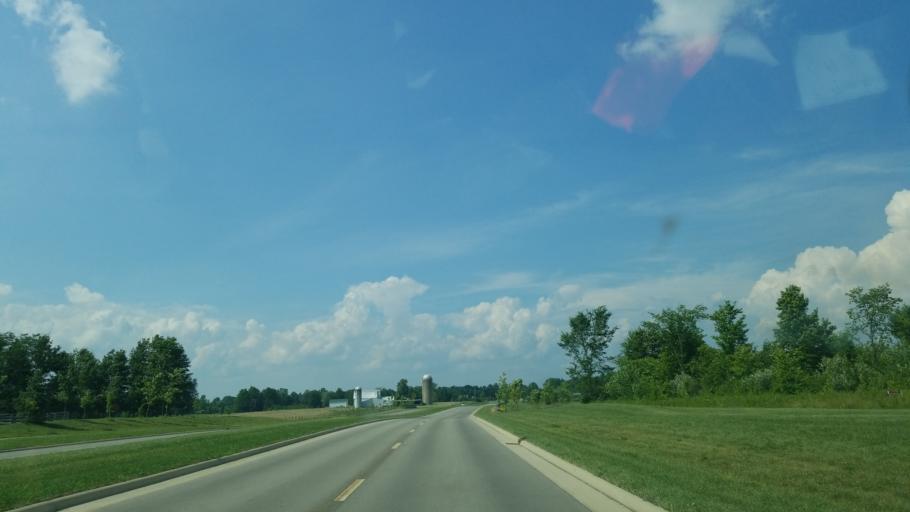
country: US
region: Ohio
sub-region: Delaware County
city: Delaware
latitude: 40.2391
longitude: -83.0948
